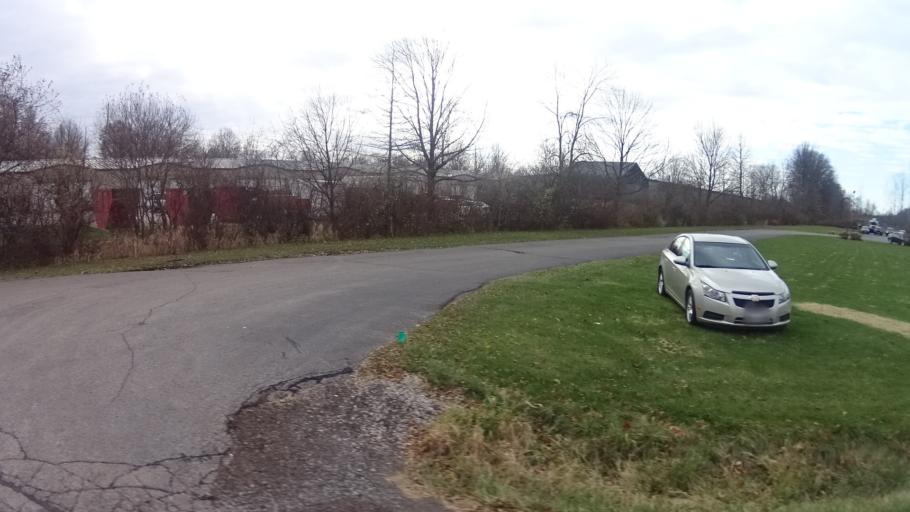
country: US
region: Ohio
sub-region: Lorain County
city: North Ridgeville
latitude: 41.3767
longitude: -82.0046
